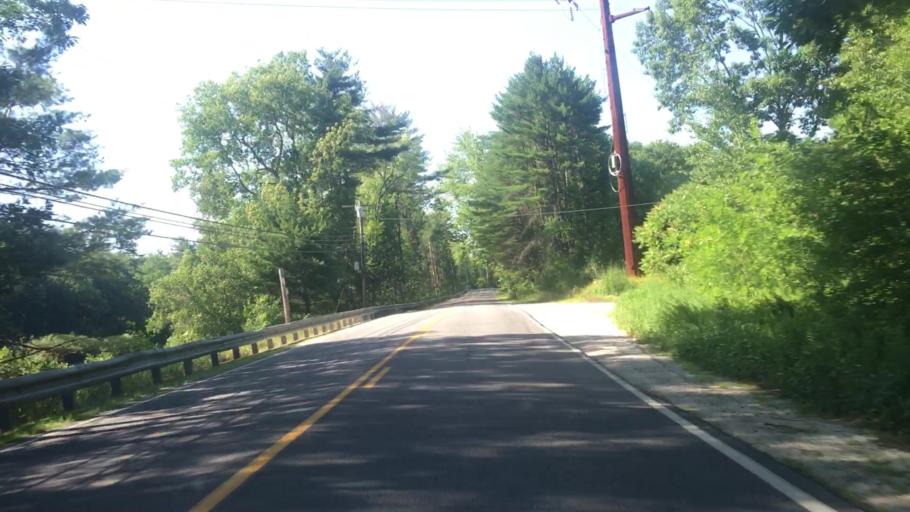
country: US
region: Maine
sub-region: York County
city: Hollis Center
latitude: 43.6517
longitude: -70.5958
